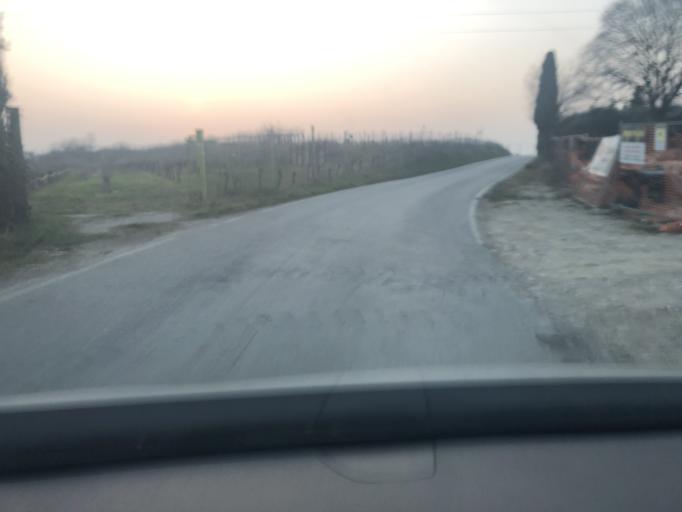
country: IT
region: Veneto
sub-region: Provincia di Verona
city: Sommacampagna
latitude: 45.3906
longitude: 10.8069
